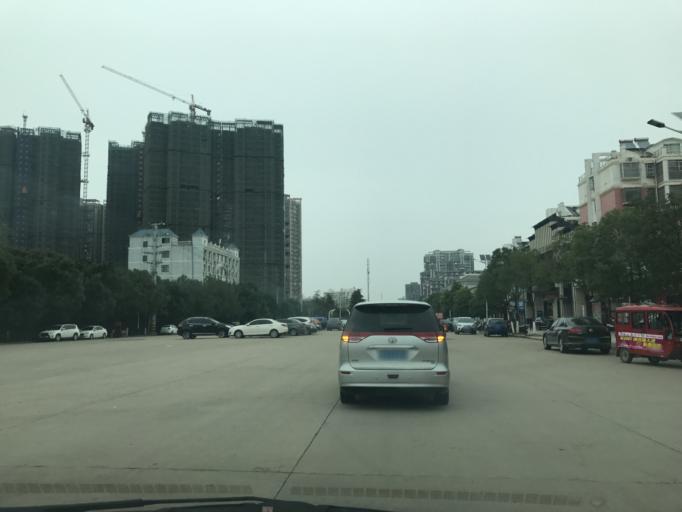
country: CN
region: Hubei
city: Anlu
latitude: 31.2645
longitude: 113.7044
